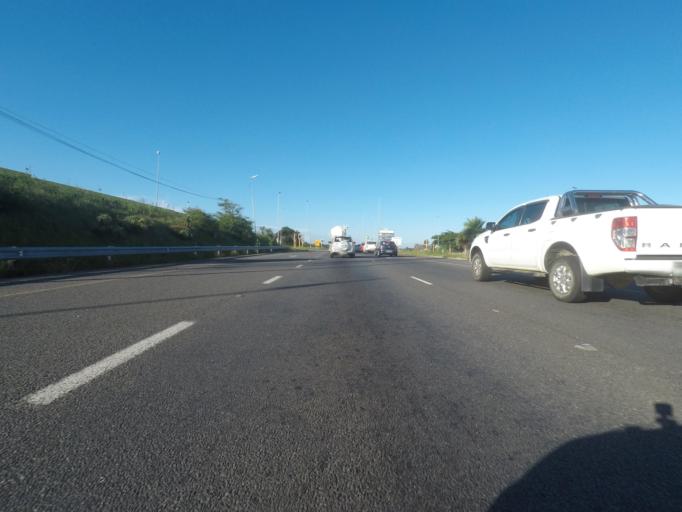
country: ZA
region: Eastern Cape
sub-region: Buffalo City Metropolitan Municipality
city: East London
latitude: -33.0391
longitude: 27.8319
